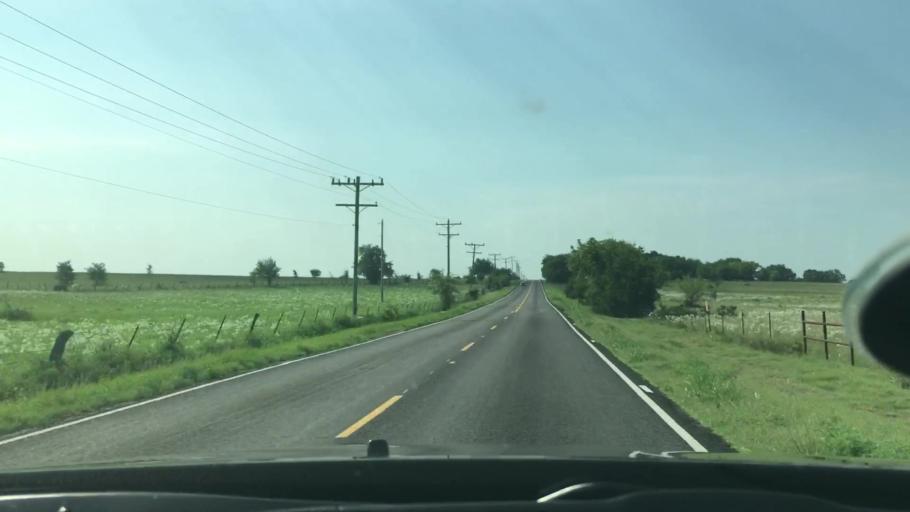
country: US
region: Oklahoma
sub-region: Bryan County
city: Durant
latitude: 34.1333
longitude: -96.4932
